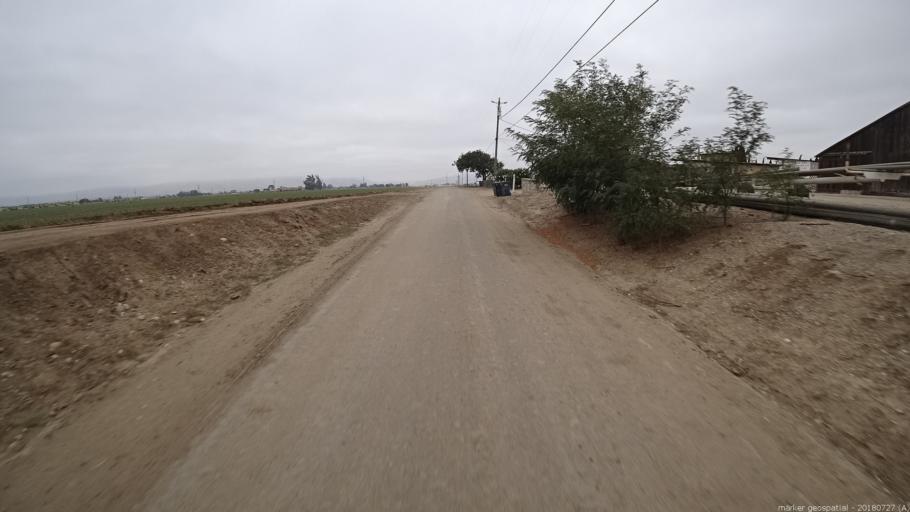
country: US
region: California
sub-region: Monterey County
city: Greenfield
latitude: 36.3440
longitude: -121.2339
